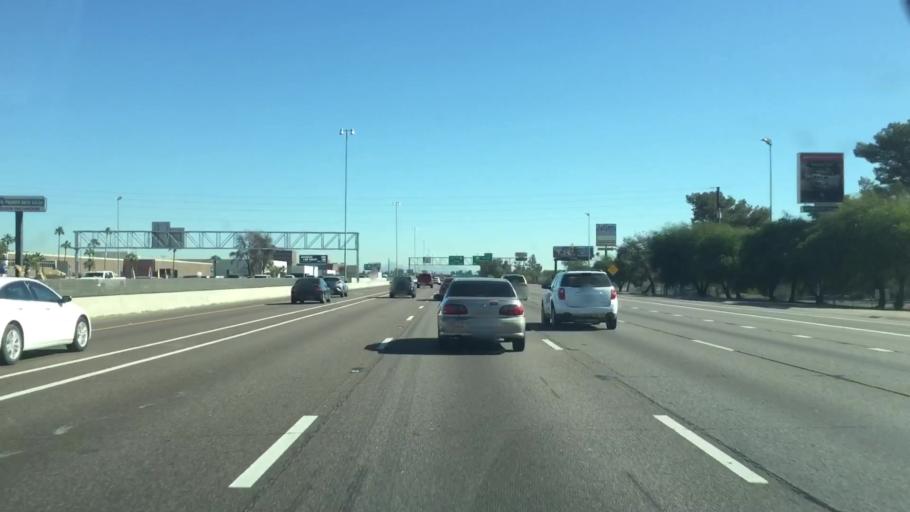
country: US
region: Arizona
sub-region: Maricopa County
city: Tempe Junction
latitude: 33.4107
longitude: -111.9920
